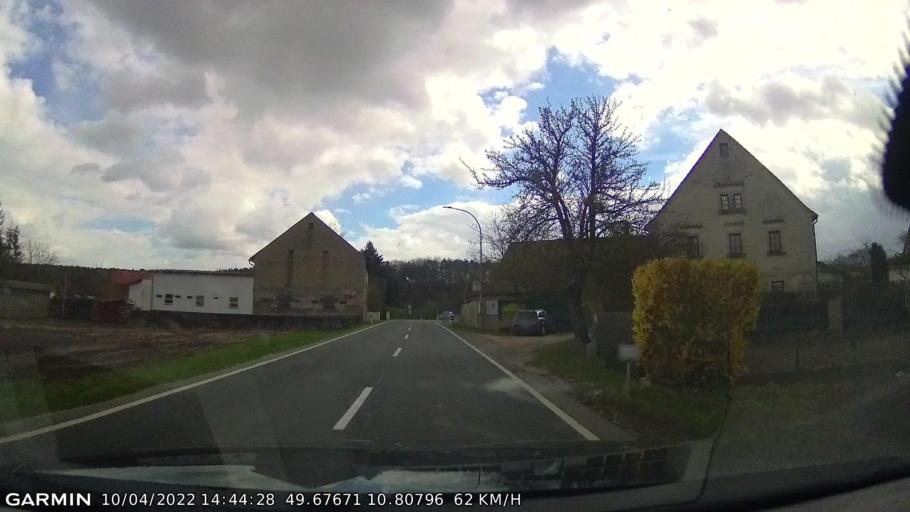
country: DE
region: Bavaria
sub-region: Regierungsbezirk Mittelfranken
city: Hochstadt an der Aisch
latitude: 49.6766
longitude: 10.8080
